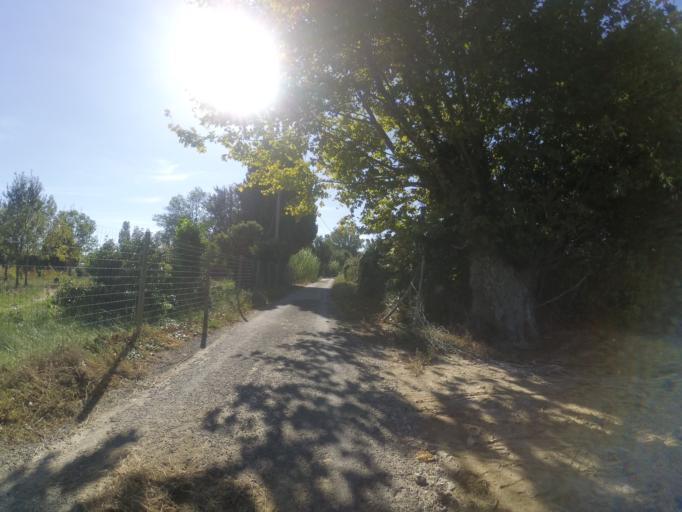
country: FR
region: Languedoc-Roussillon
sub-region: Departement des Pyrenees-Orientales
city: Pezilla-la-Riviere
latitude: 42.6893
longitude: 2.7676
